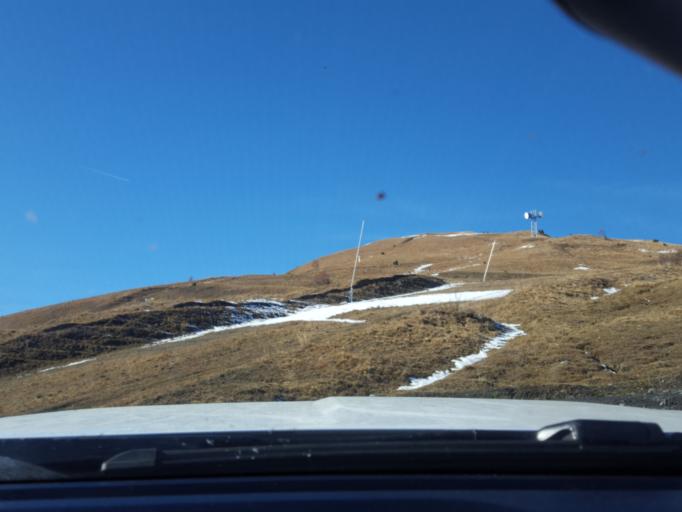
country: FR
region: Rhone-Alpes
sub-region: Departement de la Savoie
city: Saint-Jean-de-Maurienne
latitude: 45.2191
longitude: 6.2702
